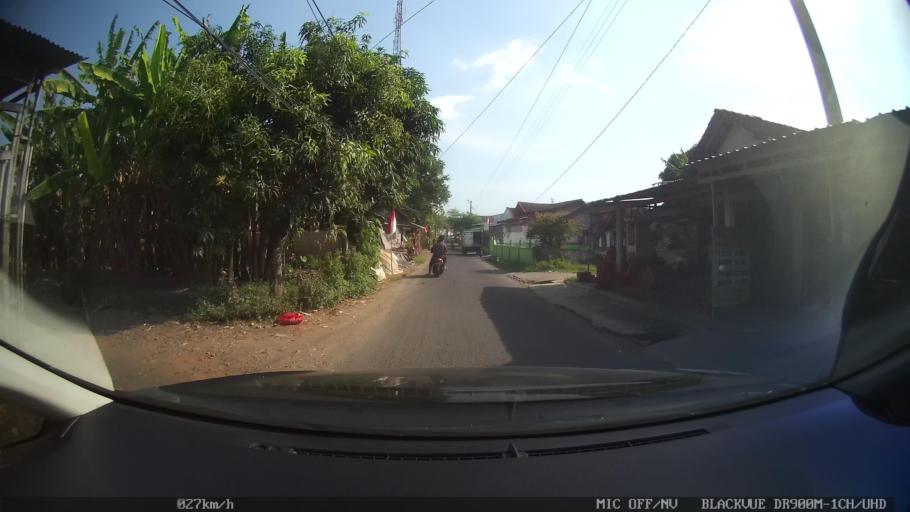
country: ID
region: Daerah Istimewa Yogyakarta
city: Kasihan
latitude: -7.8411
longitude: 110.3331
